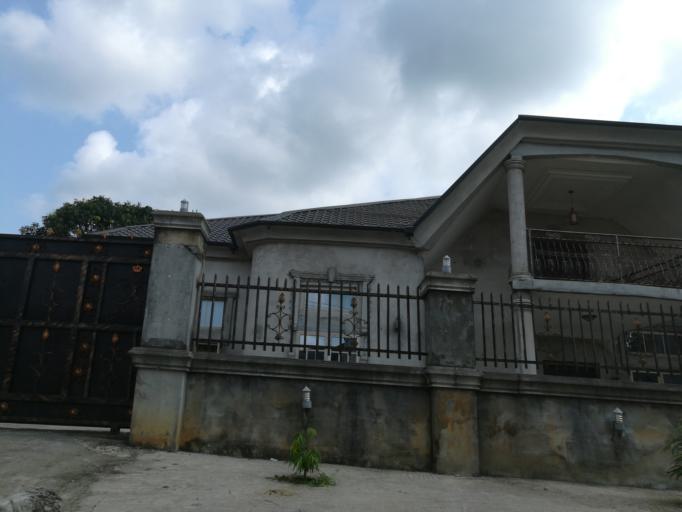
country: NG
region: Rivers
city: Okrika
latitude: 4.7429
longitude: 7.1151
